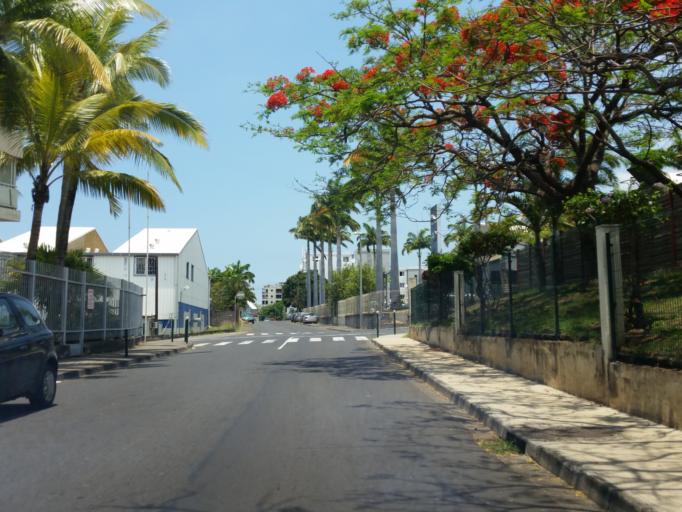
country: RE
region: Reunion
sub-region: Reunion
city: Saint-Denis
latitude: -20.8944
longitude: 55.4745
